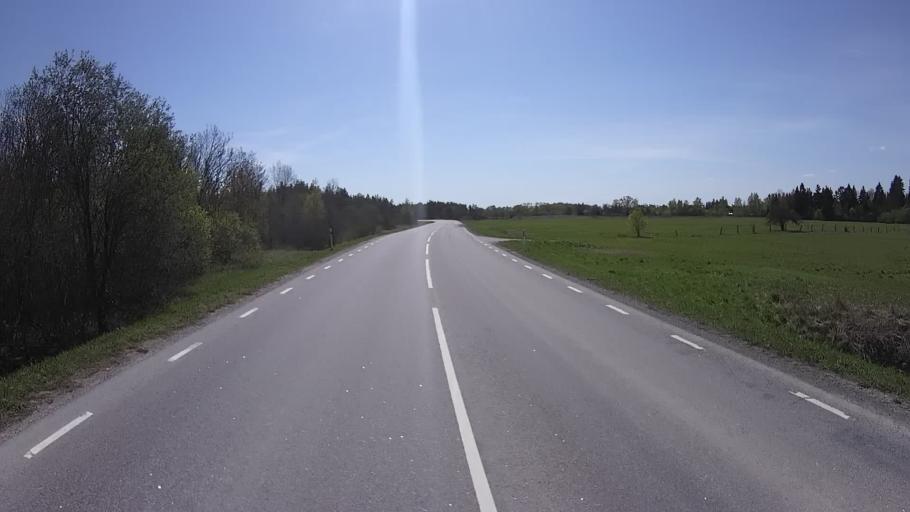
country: EE
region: Harju
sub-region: Keila linn
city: Keila
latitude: 59.3029
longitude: 24.3251
